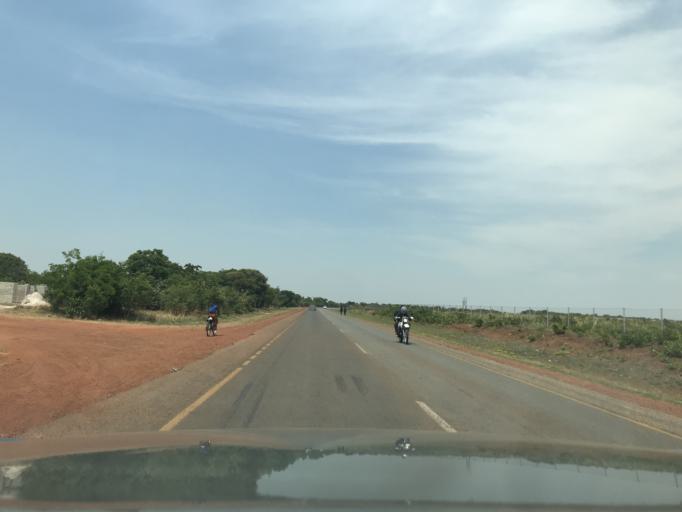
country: ZM
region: Northern
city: Kasama
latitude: -10.2196
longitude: 31.1385
